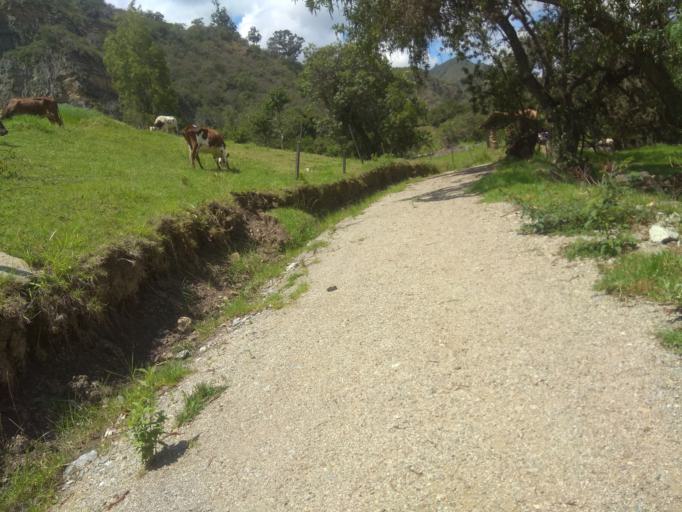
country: CO
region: Boyaca
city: Socha Viejo
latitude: 6.0000
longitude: -72.7125
